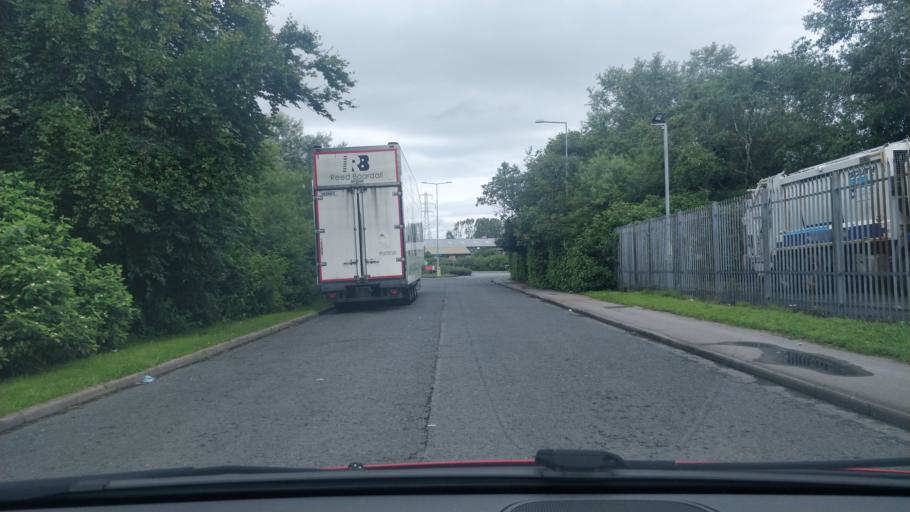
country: GB
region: England
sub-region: Lancashire
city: Leyland
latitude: 53.6999
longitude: -2.7266
